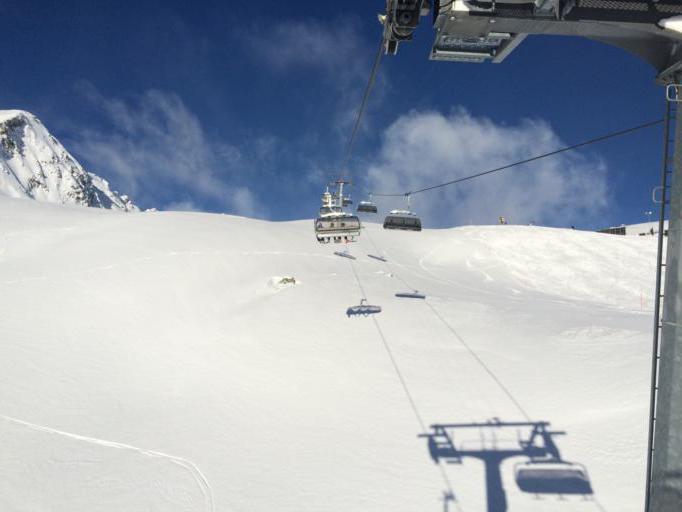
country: CH
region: Grisons
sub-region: Praettigau/Davos District
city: Davos
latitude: 46.8227
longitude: 9.8182
